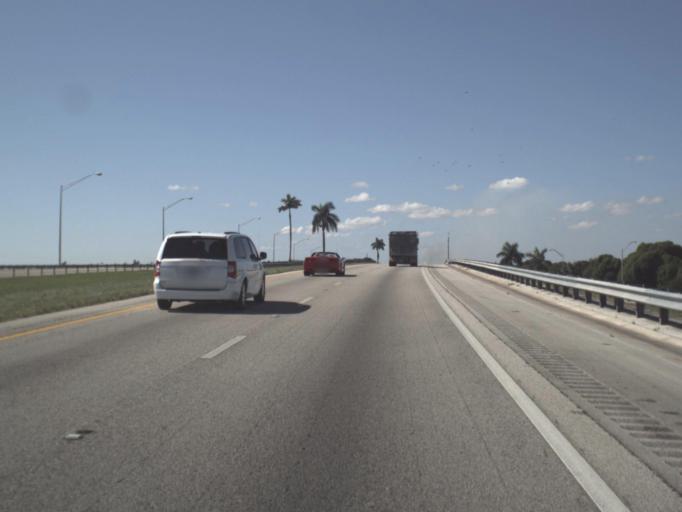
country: US
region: Florida
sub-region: Miami-Dade County
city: Naranja
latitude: 25.5123
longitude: -80.4107
